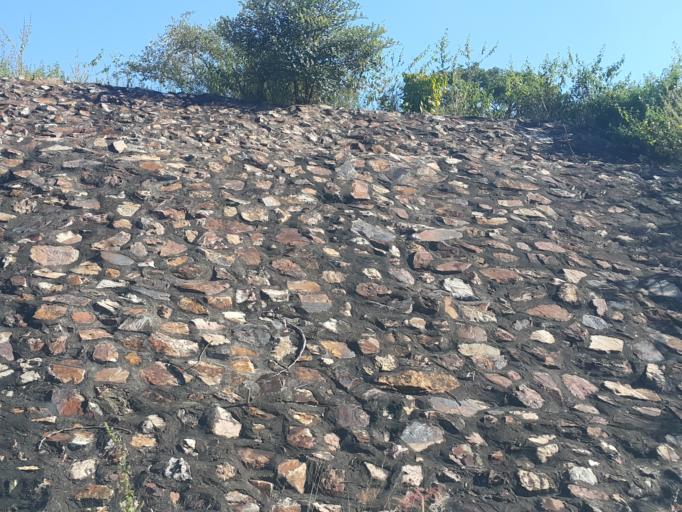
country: TH
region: Chiang Mai
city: San Sai
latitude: 18.9244
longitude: 99.1145
